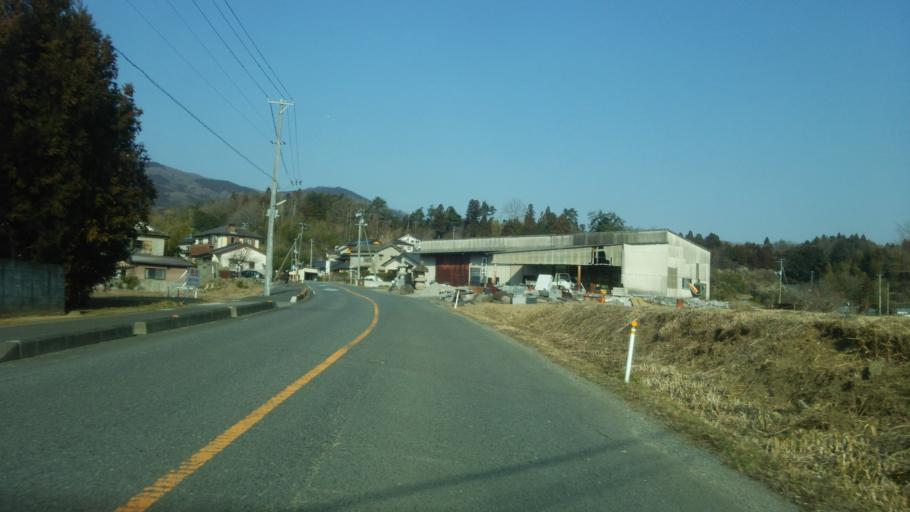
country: JP
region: Fukushima
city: Iwaki
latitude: 37.0438
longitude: 140.8064
